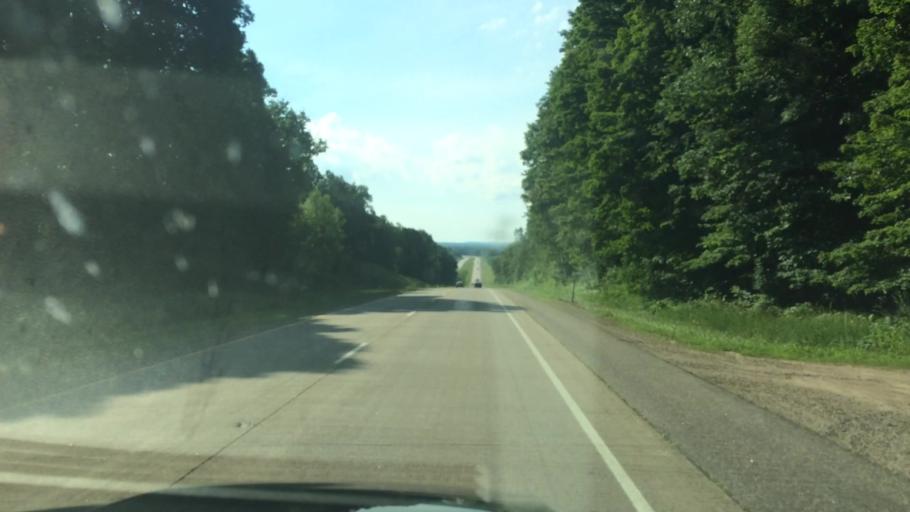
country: US
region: Wisconsin
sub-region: Shawano County
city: Wittenberg
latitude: 44.8202
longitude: -89.0552
